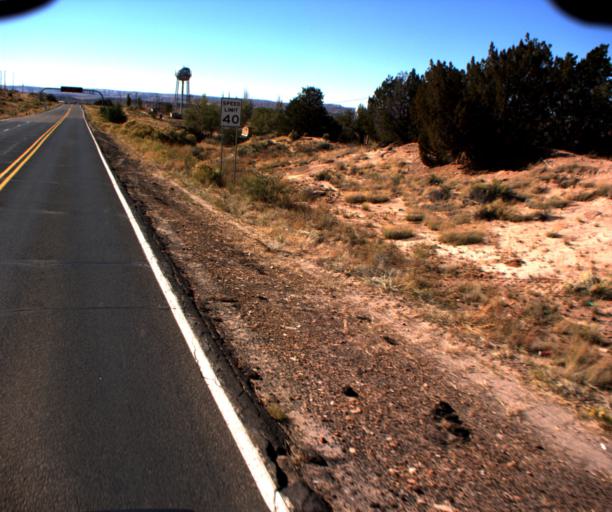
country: US
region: Arizona
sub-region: Apache County
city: Ganado
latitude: 35.7099
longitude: -109.5278
